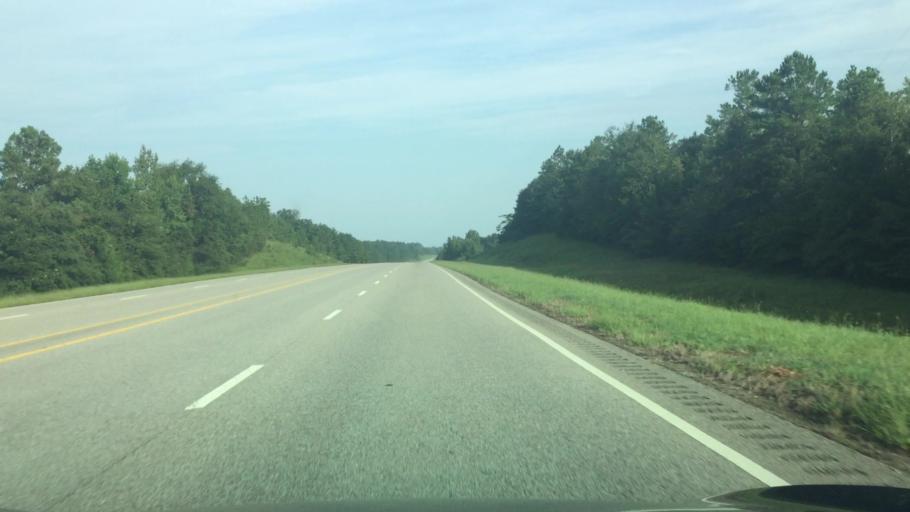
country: US
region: Alabama
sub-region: Covington County
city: Andalusia
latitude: 31.4457
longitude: -86.6173
